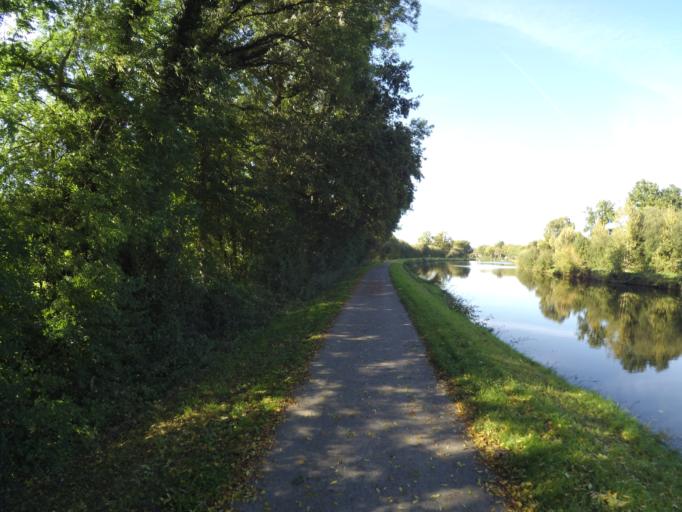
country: FR
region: Brittany
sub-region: Departement du Morbihan
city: Saint-Martin-sur-Oust
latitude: 47.7405
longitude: -2.2585
